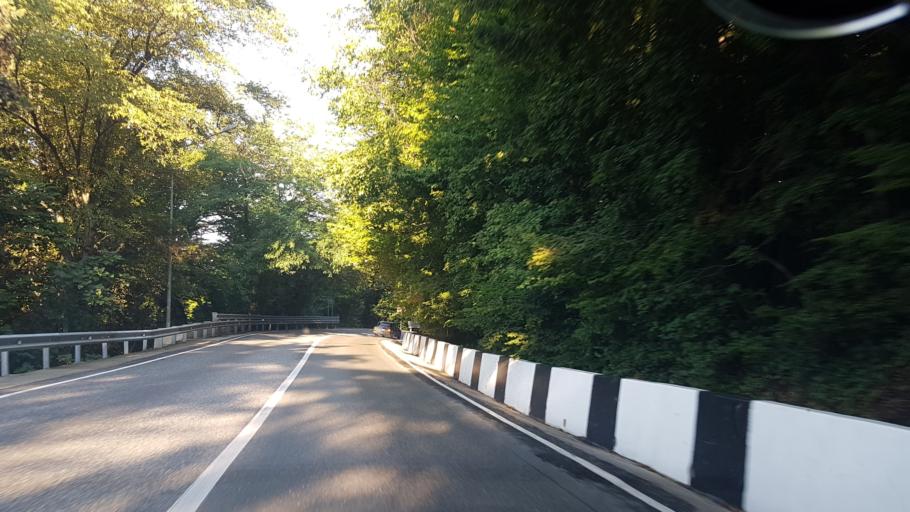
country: RU
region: Krasnodarskiy
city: Dagomys
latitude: 43.6690
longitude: 39.6266
